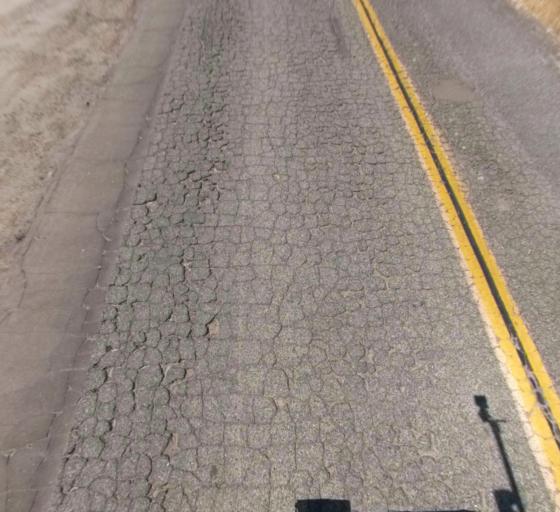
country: US
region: California
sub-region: Madera County
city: Parkwood
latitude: 36.9160
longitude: -120.0193
